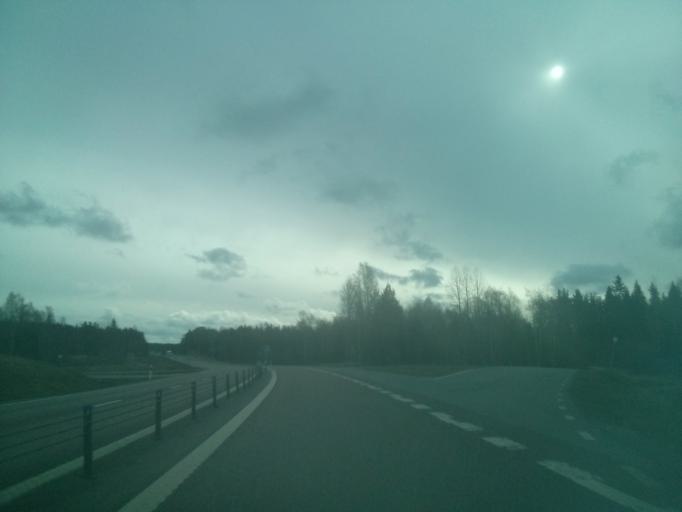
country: SE
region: Vaesternorrland
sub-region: Timra Kommun
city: Soraker
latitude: 62.5348
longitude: 17.5395
